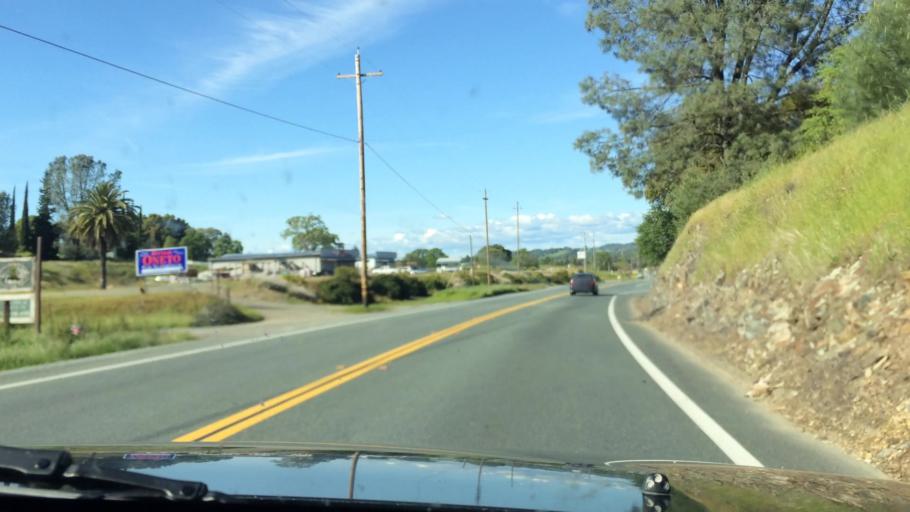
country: US
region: California
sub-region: Amador County
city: Plymouth
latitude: 38.4649
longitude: -120.8564
